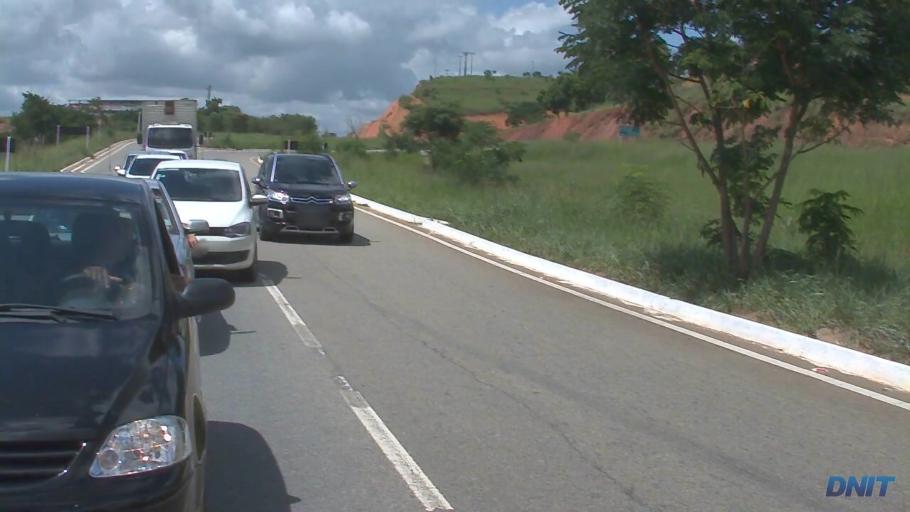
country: BR
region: Minas Gerais
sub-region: Governador Valadares
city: Governador Valadares
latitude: -18.9055
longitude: -42.0035
